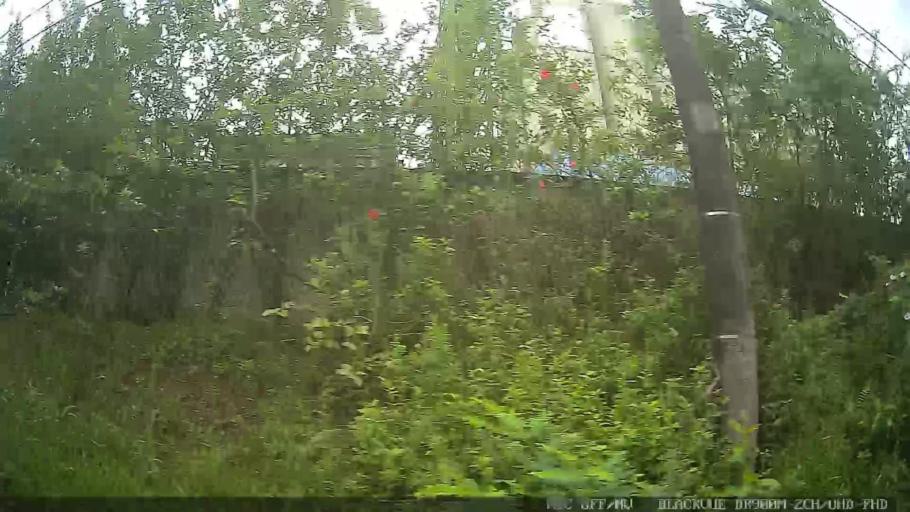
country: BR
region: Sao Paulo
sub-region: Maua
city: Maua
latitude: -23.6404
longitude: -46.4665
